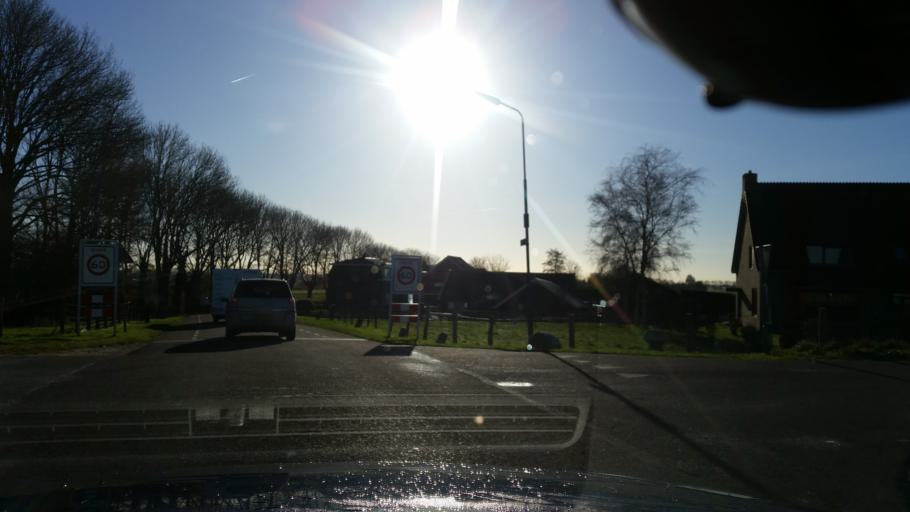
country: NL
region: North Holland
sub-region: Gemeente Ouder-Amstel
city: Ouderkerk aan de Amstel
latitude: 52.2530
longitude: 4.9025
